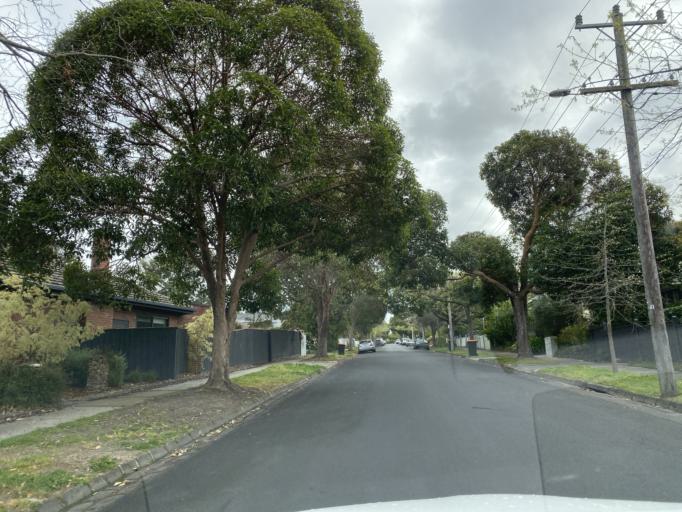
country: AU
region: Victoria
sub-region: Boroondara
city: Canterbury
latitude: -37.8319
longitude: 145.0916
